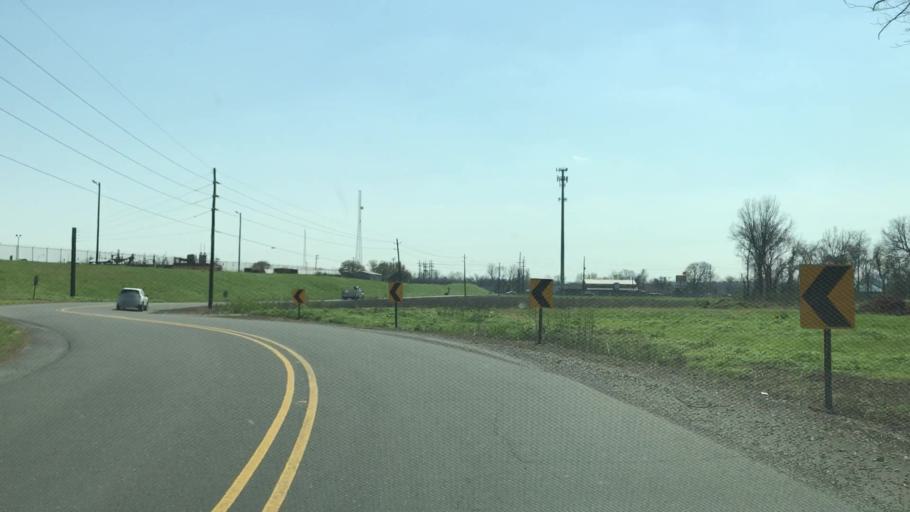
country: US
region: Louisiana
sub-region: Bossier Parish
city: Bossier City
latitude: 32.4043
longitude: -93.6912
